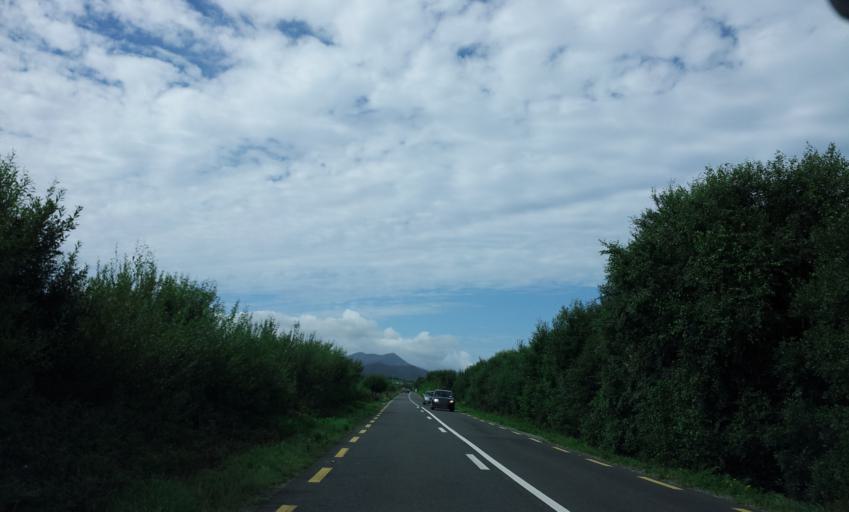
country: IE
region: Munster
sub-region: Ciarrai
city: Killorglin
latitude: 52.0835
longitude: -9.8675
